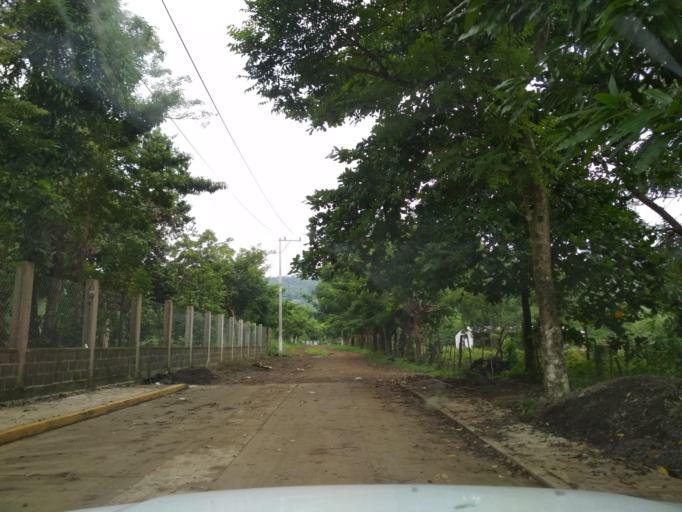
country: MX
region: Veracruz
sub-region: San Andres Tuxtla
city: Matacapan
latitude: 18.4433
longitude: -95.1777
